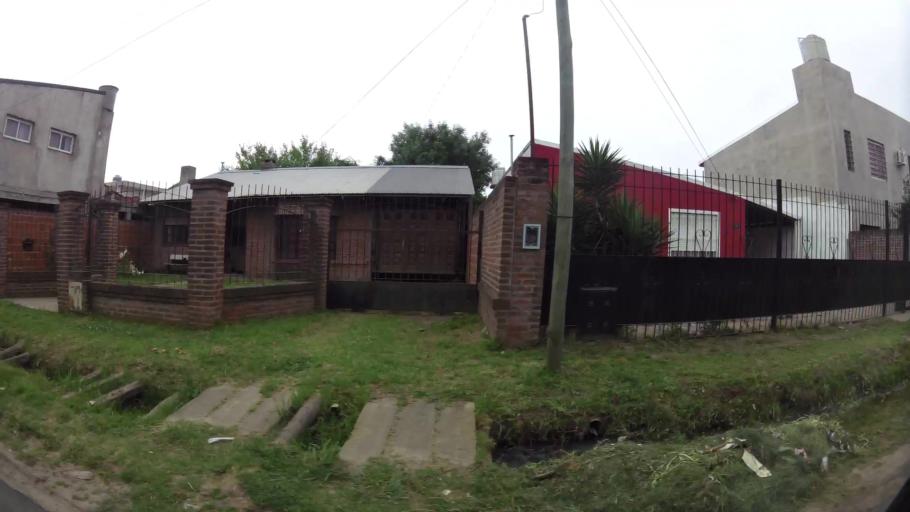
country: AR
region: Buenos Aires
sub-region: Partido de Campana
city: Campana
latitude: -34.2092
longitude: -58.9356
